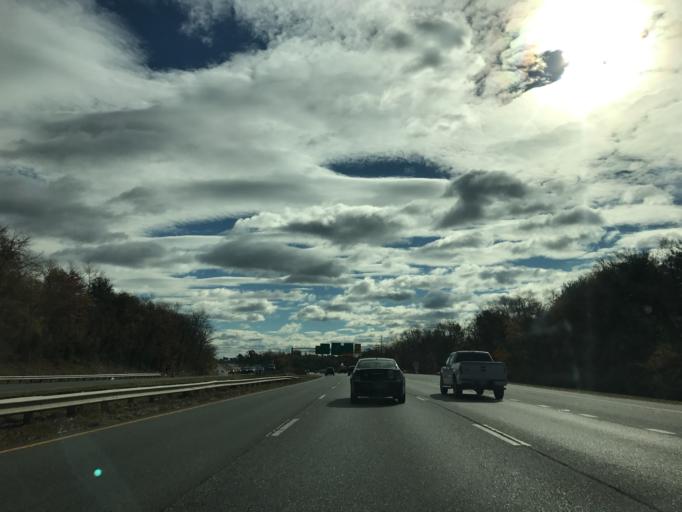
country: US
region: Maryland
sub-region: Anne Arundel County
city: Linthicum
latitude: 39.2130
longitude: -76.6532
